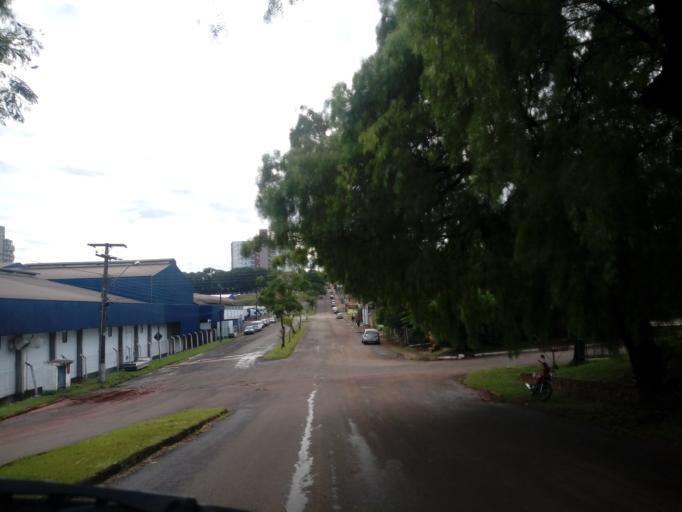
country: BR
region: Santa Catarina
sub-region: Chapeco
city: Chapeco
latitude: -27.1061
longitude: -52.6289
